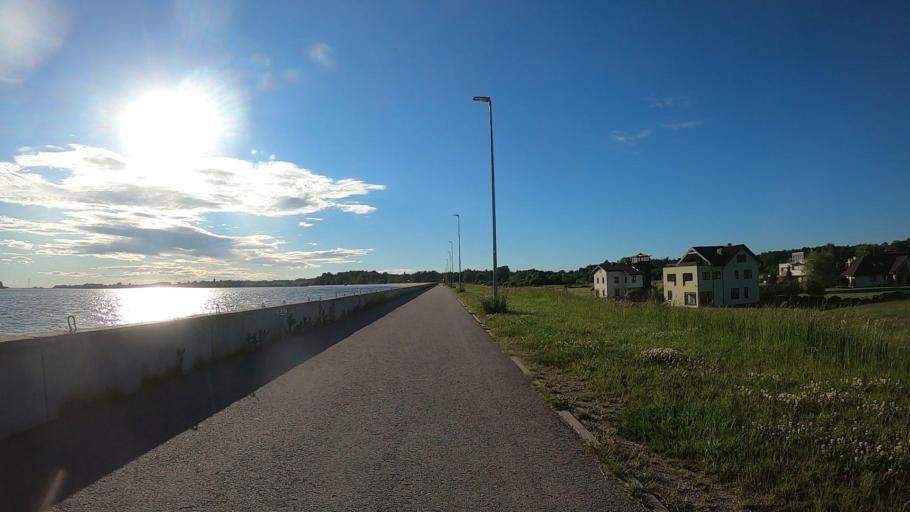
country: LV
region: Ikskile
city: Ikskile
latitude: 56.8377
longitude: 24.4690
